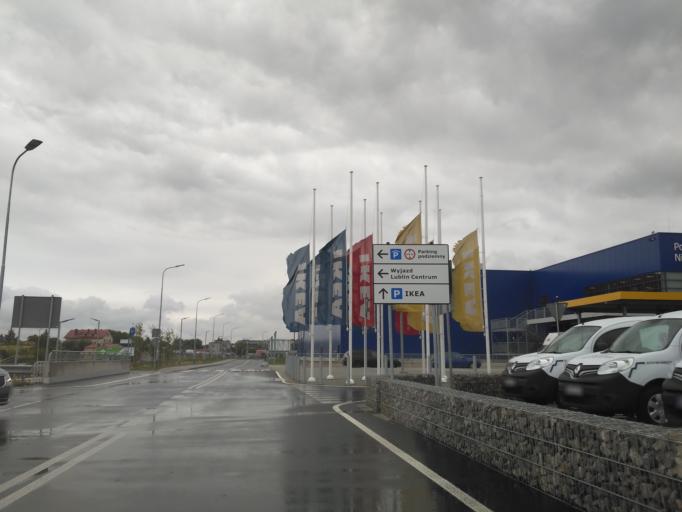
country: PL
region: Lublin Voivodeship
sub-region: Powiat lubelski
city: Lublin
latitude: 51.2829
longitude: 22.5742
